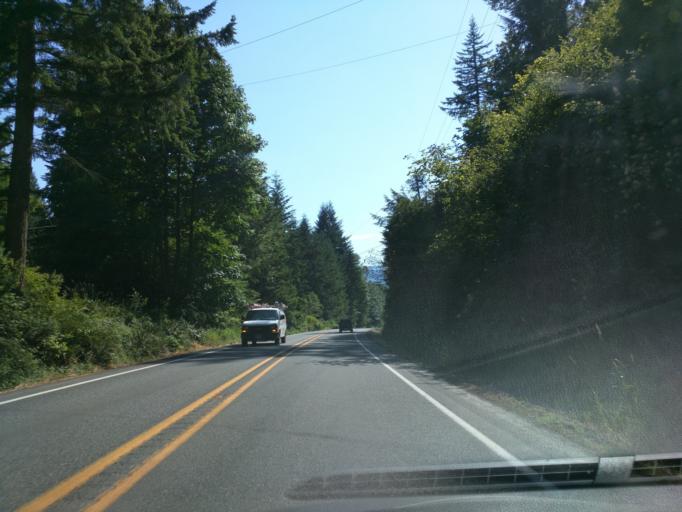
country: US
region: Washington
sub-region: Whatcom County
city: Peaceful Valley
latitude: 48.8328
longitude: -122.1714
